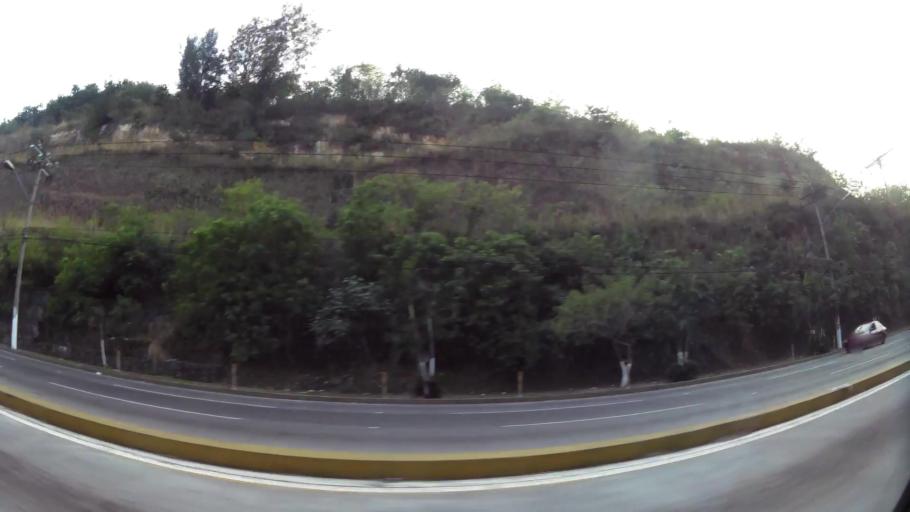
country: SV
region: San Salvador
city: San Salvador
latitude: 13.6826
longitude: -89.2171
